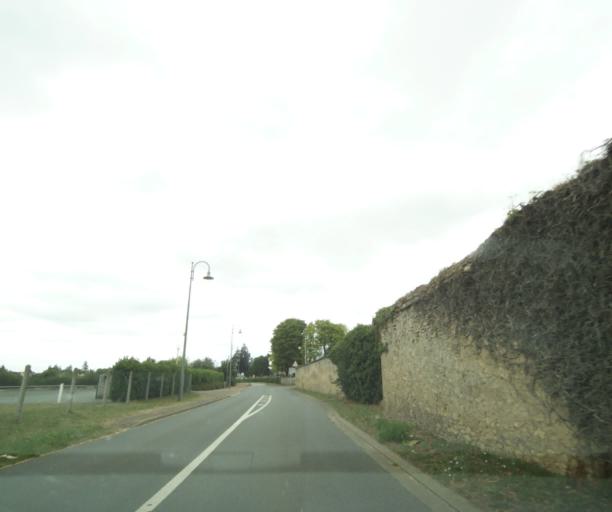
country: FR
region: Pays de la Loire
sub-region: Departement de la Sarthe
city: Precigne
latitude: 47.7709
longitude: -0.3226
